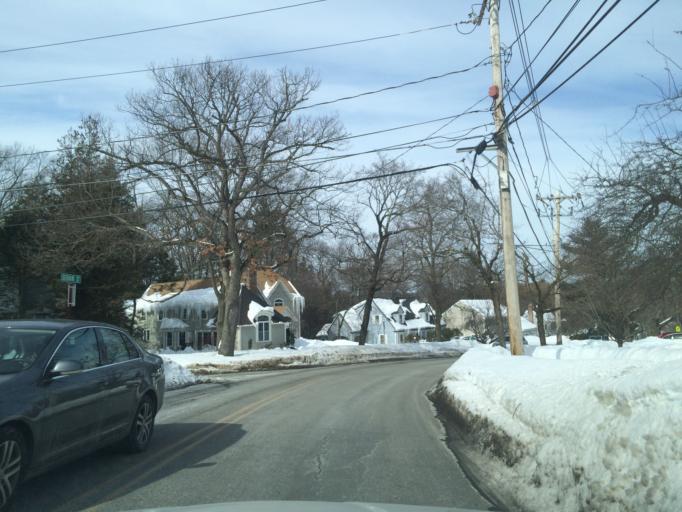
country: US
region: Massachusetts
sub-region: Middlesex County
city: Newton
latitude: 42.3100
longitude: -71.2026
